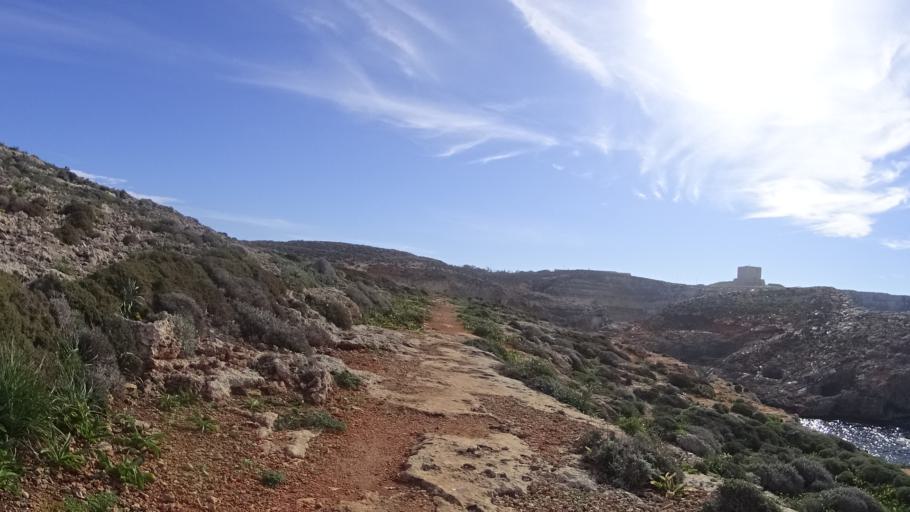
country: MT
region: Il-Qala
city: Qala
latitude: 36.0113
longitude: 14.3263
